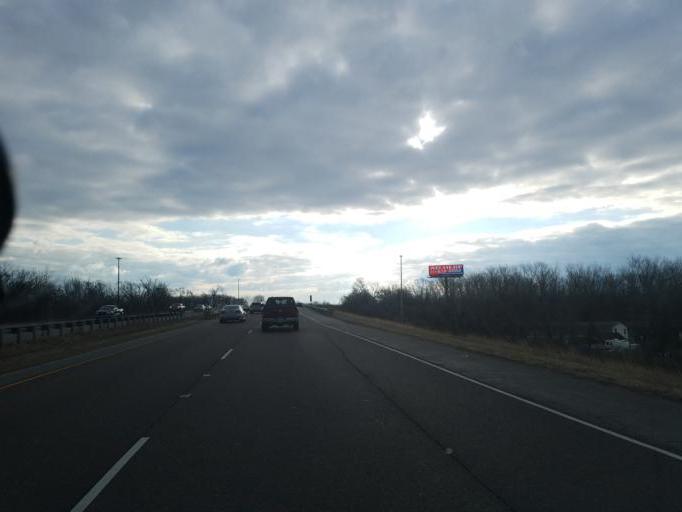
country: US
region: Illinois
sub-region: Madison County
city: Mitchell
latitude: 38.7665
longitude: -90.1181
